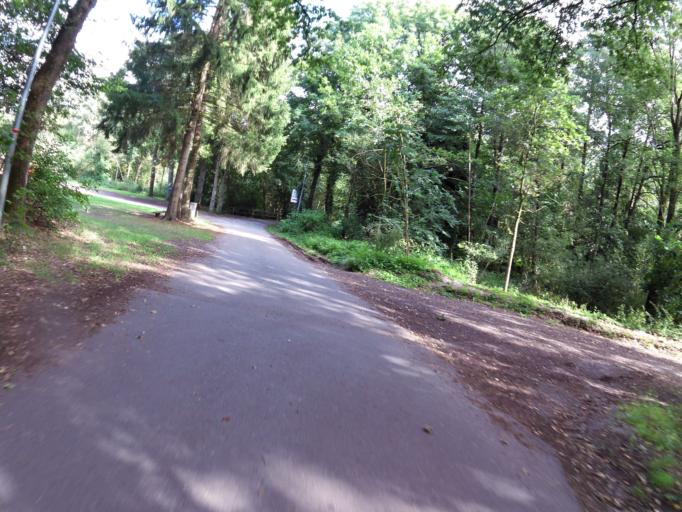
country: DE
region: Lower Saxony
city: Heeslingen
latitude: 53.2956
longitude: 9.3776
